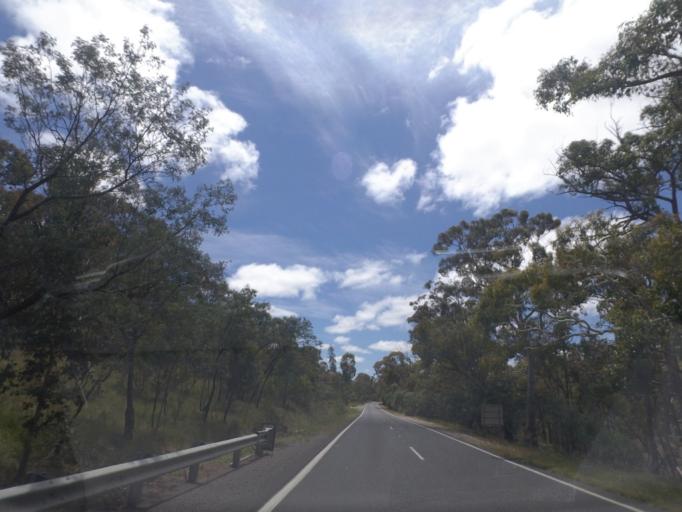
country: AU
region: Victoria
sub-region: Mount Alexander
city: Castlemaine
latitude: -37.3029
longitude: 144.1633
